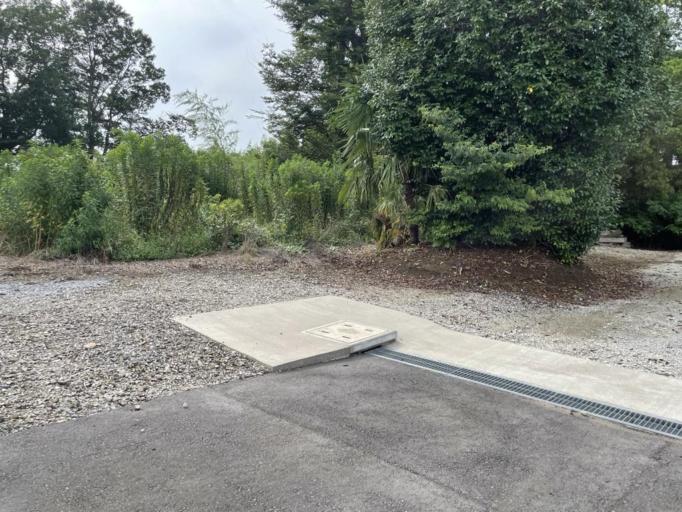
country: JP
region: Chiba
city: Sakura
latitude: 35.7190
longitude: 140.2384
